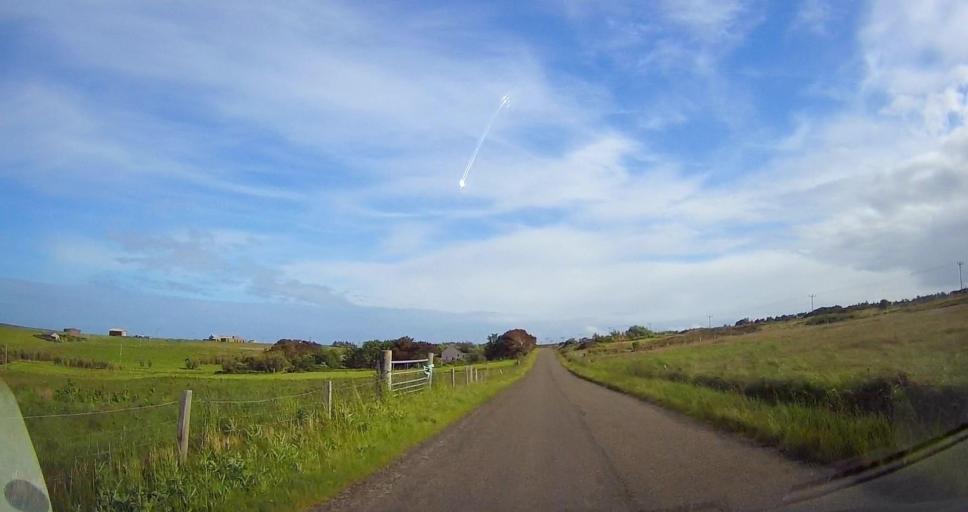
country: GB
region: Scotland
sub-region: Orkney Islands
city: Stromness
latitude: 58.8373
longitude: -3.2154
